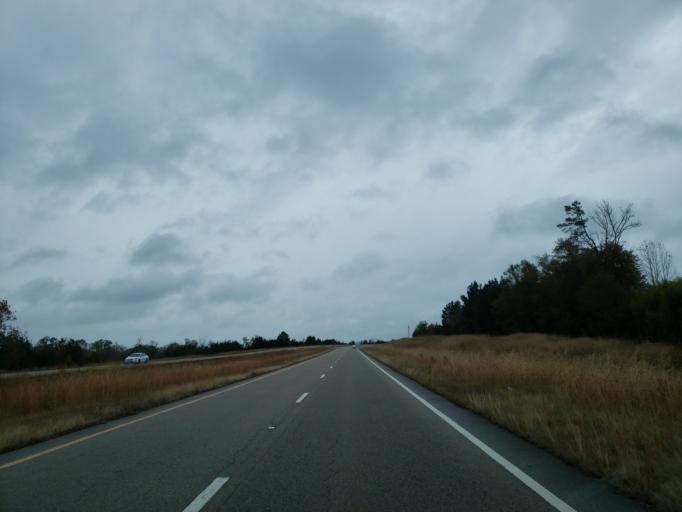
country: US
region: Mississippi
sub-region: Wayne County
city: Waynesboro
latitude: 31.7675
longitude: -88.6715
